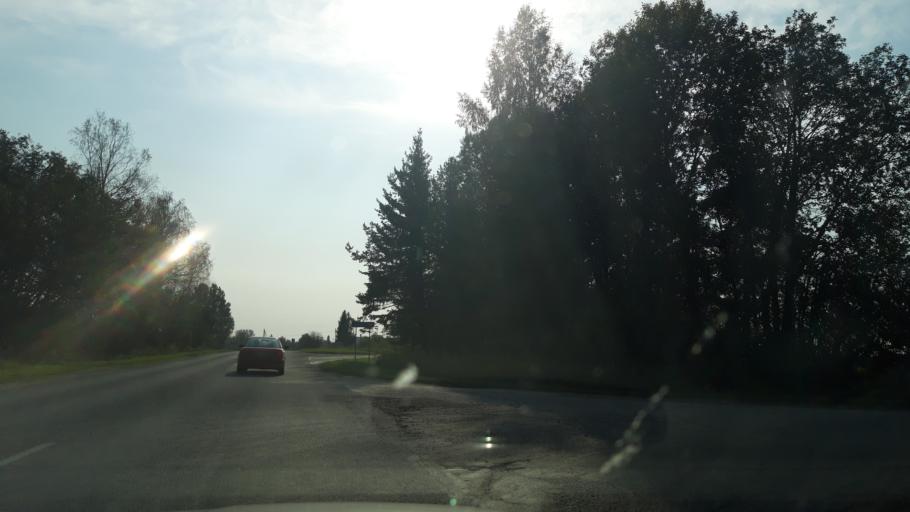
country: LV
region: Mazsalaca
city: Mazsalaca
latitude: 57.8538
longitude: 25.0532
